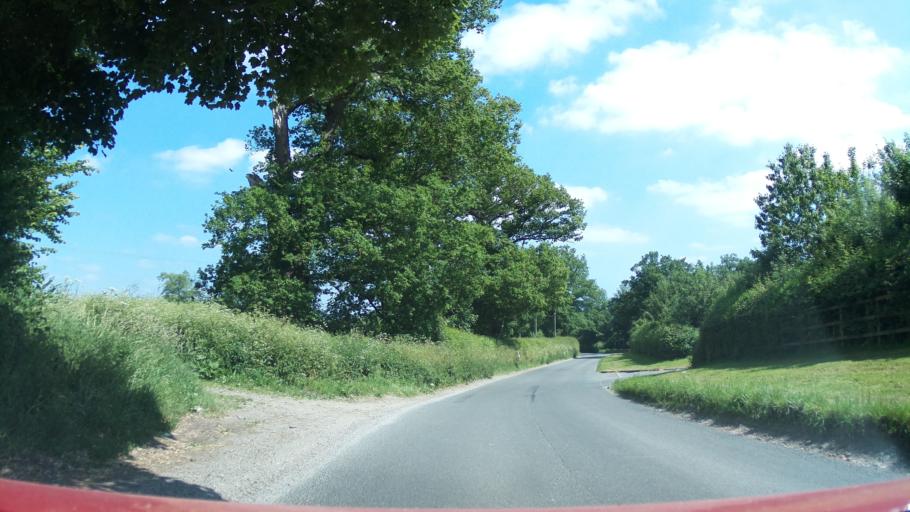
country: GB
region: England
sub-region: Wiltshire
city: Pewsey
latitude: 51.3456
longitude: -1.7851
